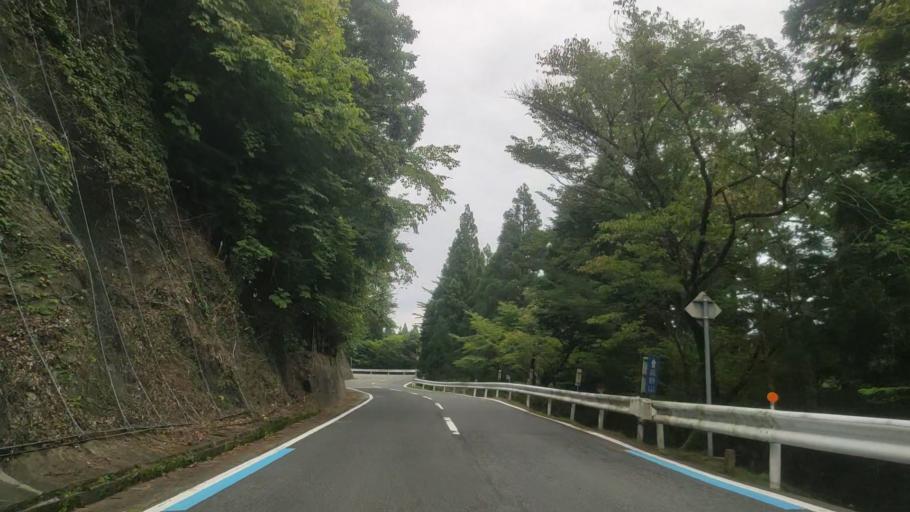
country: JP
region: Wakayama
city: Koya
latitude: 34.2206
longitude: 135.5606
